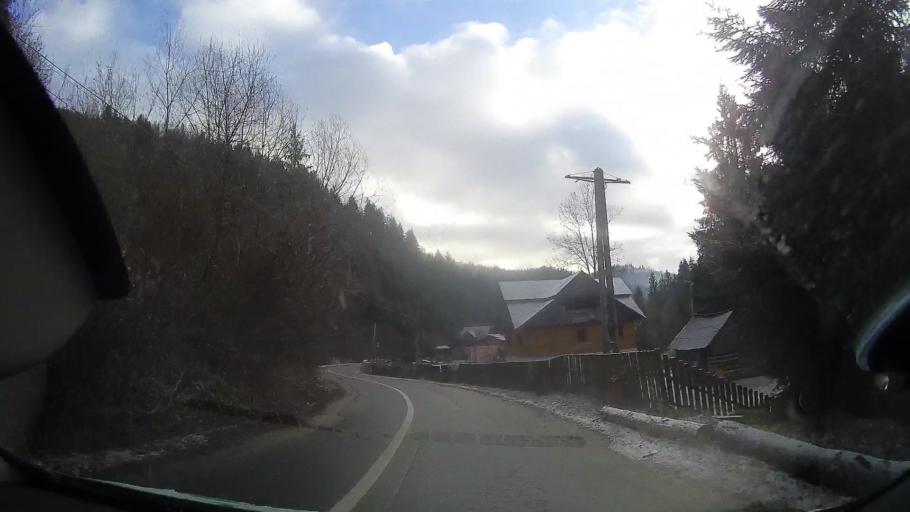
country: RO
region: Alba
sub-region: Comuna Horea
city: Horea
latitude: 46.4978
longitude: 22.9550
